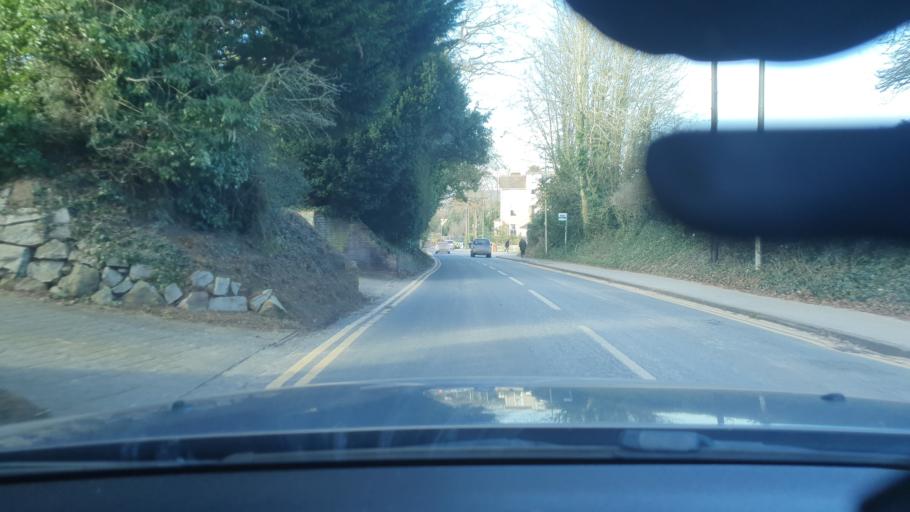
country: GB
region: England
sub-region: West Berkshire
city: Greenham
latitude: 51.3890
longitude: -1.3229
